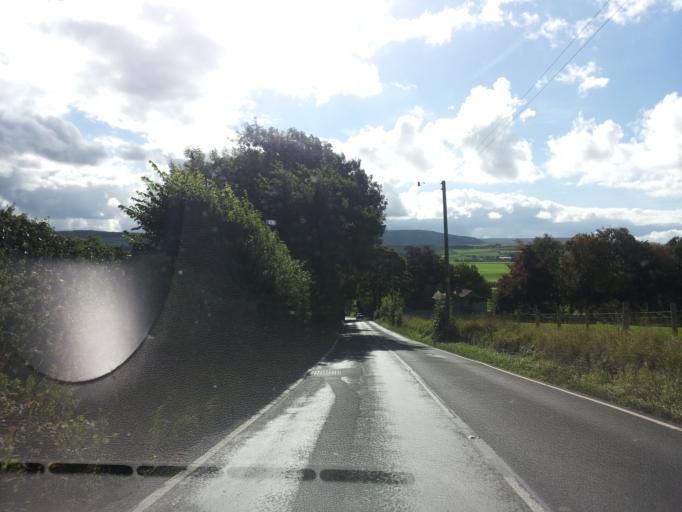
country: GB
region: England
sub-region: North Yorkshire
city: Leyburn
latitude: 54.3053
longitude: -1.8246
